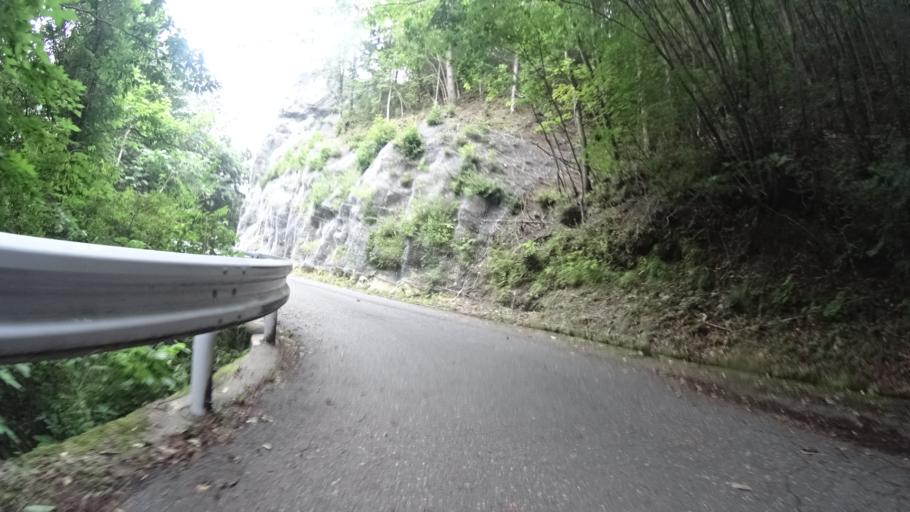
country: JP
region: Yamanashi
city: Kofu-shi
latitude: 35.8126
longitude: 138.5948
